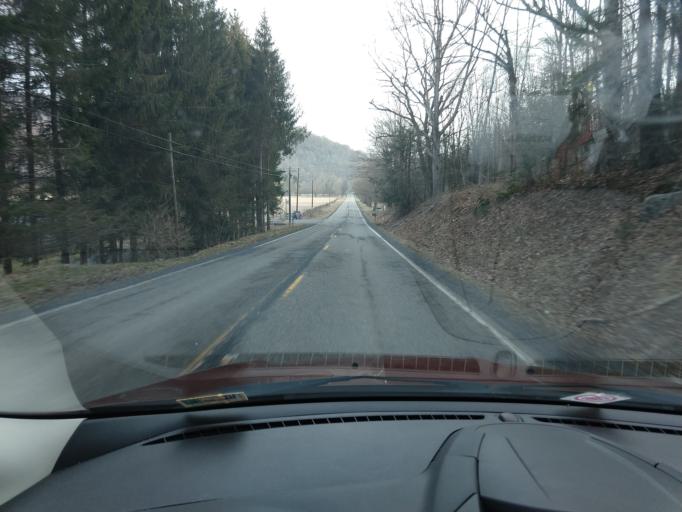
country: US
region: Virginia
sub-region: Highland County
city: Monterey
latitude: 38.4630
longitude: -79.5242
